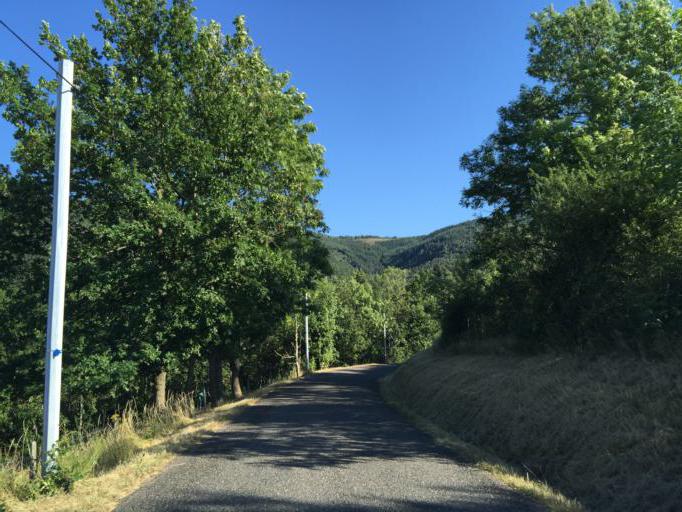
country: FR
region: Rhone-Alpes
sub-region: Departement de la Loire
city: Saint-Jean-Bonnefonds
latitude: 45.4333
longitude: 4.4789
